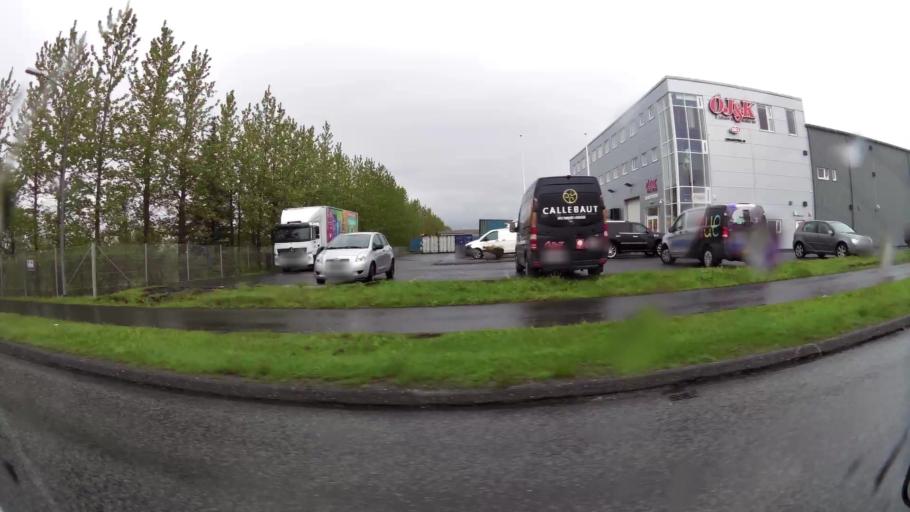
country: IS
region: Capital Region
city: Mosfellsbaer
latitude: 64.1176
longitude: -21.7906
